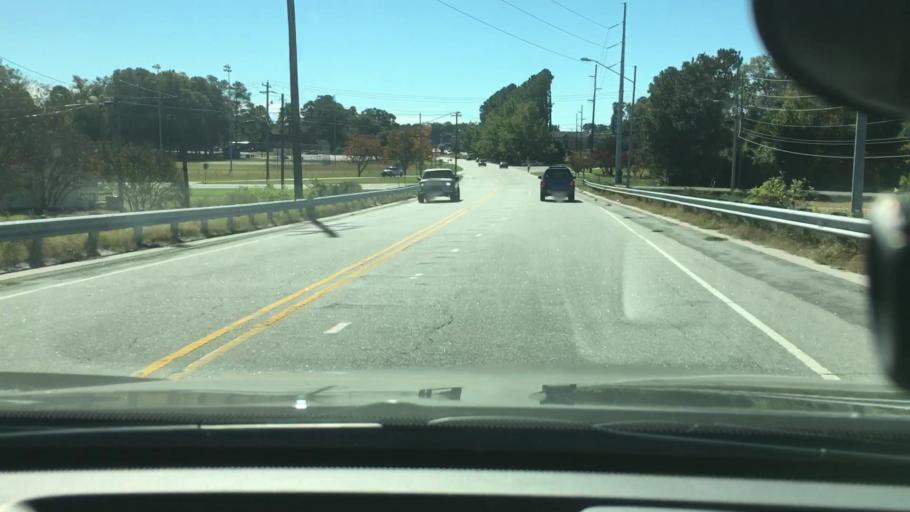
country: US
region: North Carolina
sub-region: Edgecombe County
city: Tarboro
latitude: 35.9080
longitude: -77.5628
